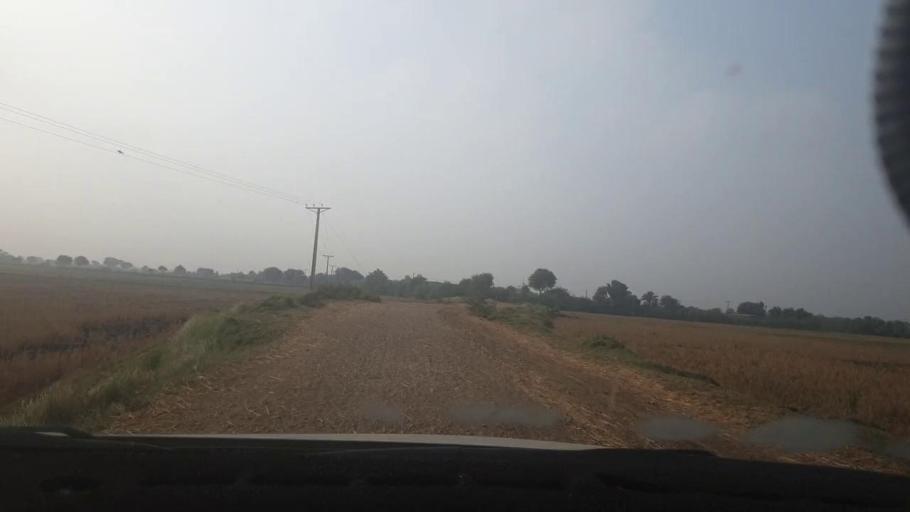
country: PK
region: Sindh
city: Tando Muhammad Khan
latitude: 25.0811
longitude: 68.5131
